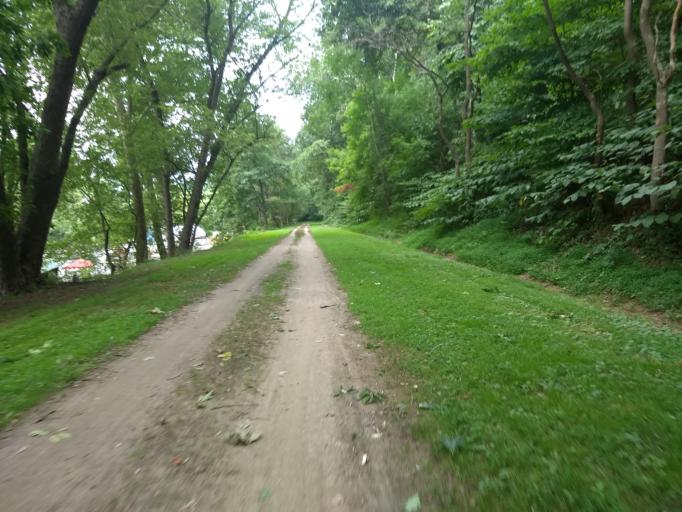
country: US
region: Pennsylvania
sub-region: Armstrong County
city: Freeport
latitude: 40.6436
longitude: -79.6861
